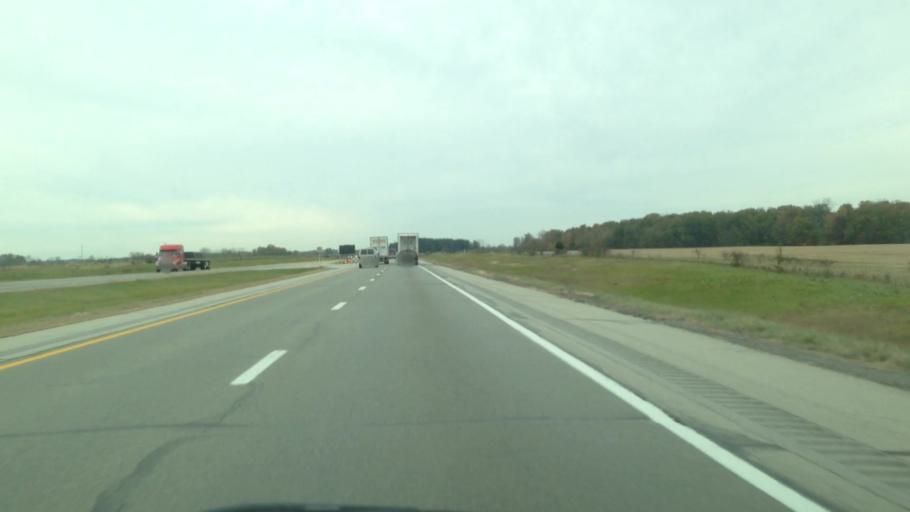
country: US
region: Ohio
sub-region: Williams County
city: Montpelier
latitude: 41.6232
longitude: -84.6951
